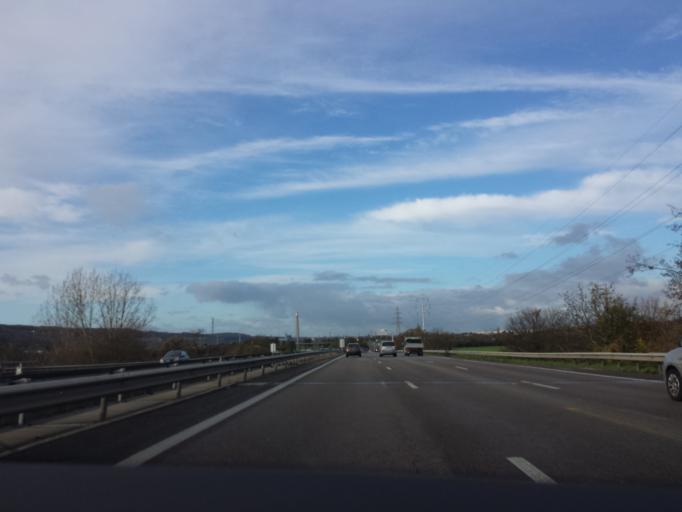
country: FR
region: Ile-de-France
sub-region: Departement des Yvelines
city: Epone
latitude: 48.9648
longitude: 1.8204
